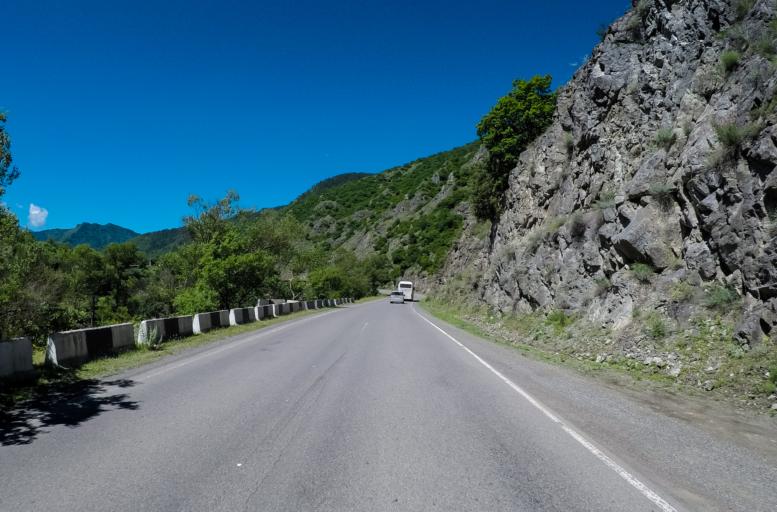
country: GE
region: Samtskhe-Javakheti
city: Borjomi
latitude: 41.7979
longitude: 43.3097
